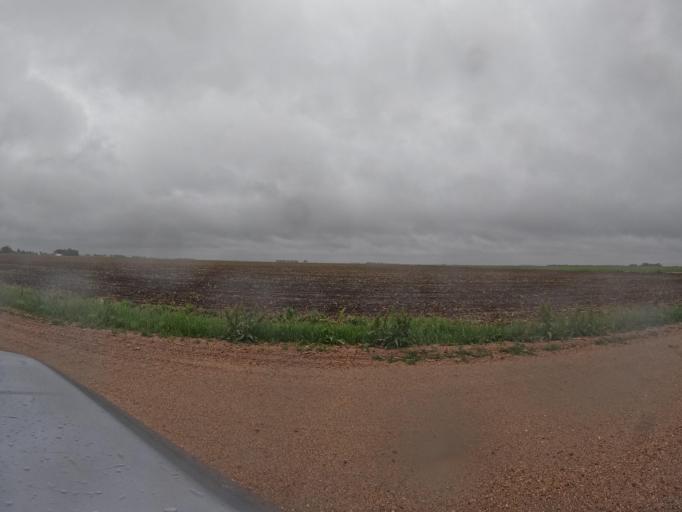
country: US
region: Nebraska
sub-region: Clay County
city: Harvard
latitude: 40.6252
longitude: -98.1040
